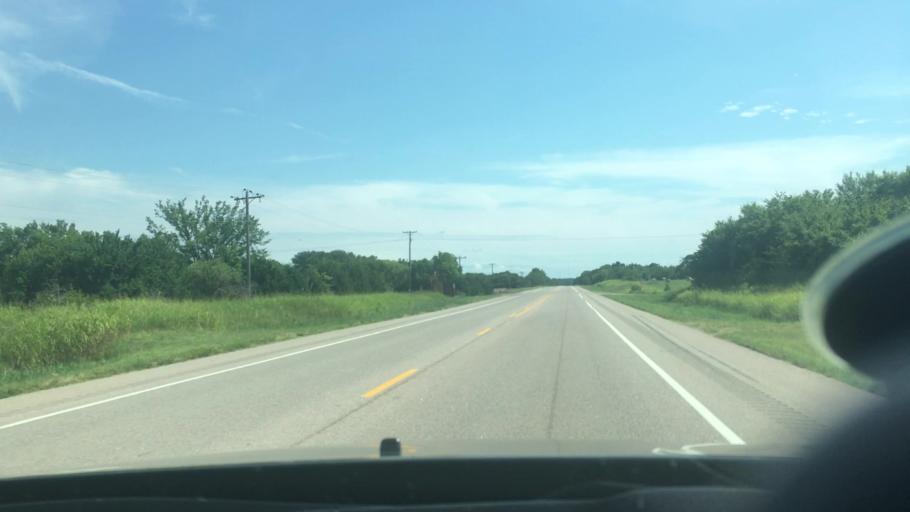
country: US
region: Oklahoma
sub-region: Seminole County
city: Konawa
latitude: 34.9721
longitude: -96.6790
